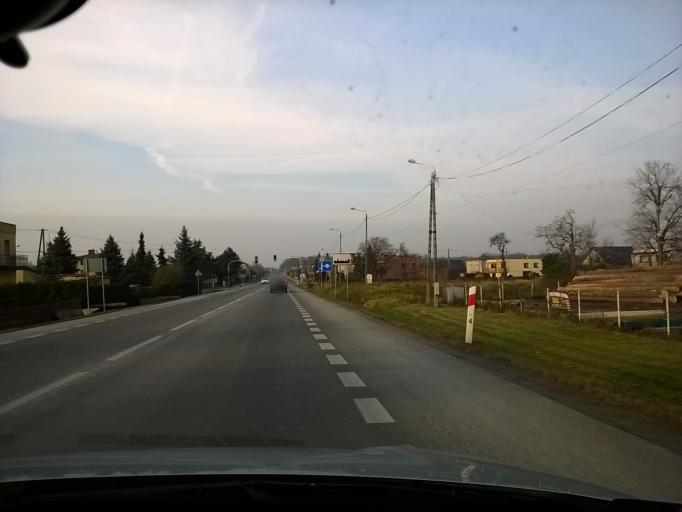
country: PL
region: Silesian Voivodeship
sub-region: Powiat gliwicki
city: Paniowki
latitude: 50.2390
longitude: 18.7714
